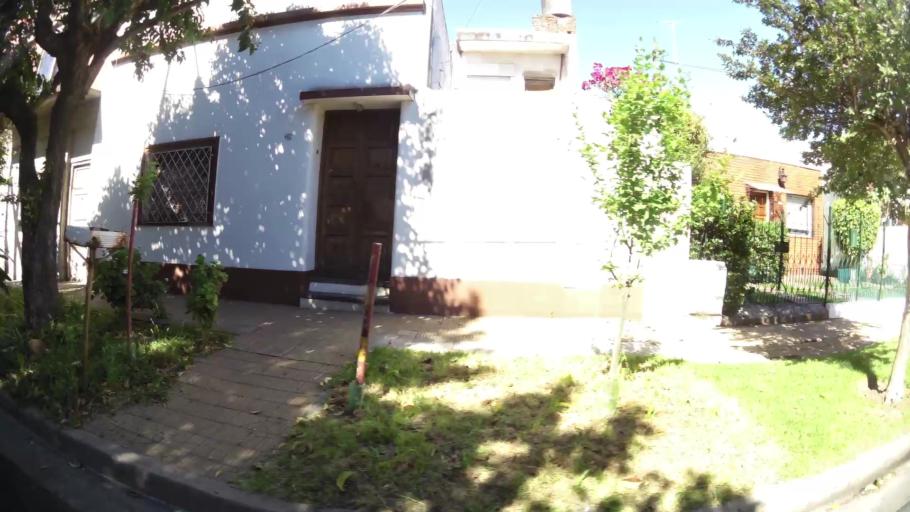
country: AR
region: Buenos Aires
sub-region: Partido de General San Martin
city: General San Martin
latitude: -34.5429
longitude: -58.5092
